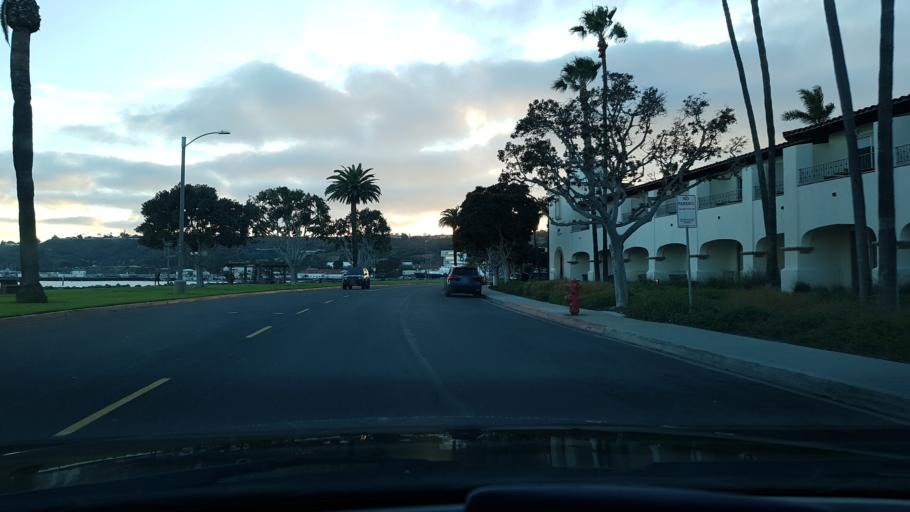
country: US
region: California
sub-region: San Diego County
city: Coronado
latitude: 32.7091
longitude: -117.2316
